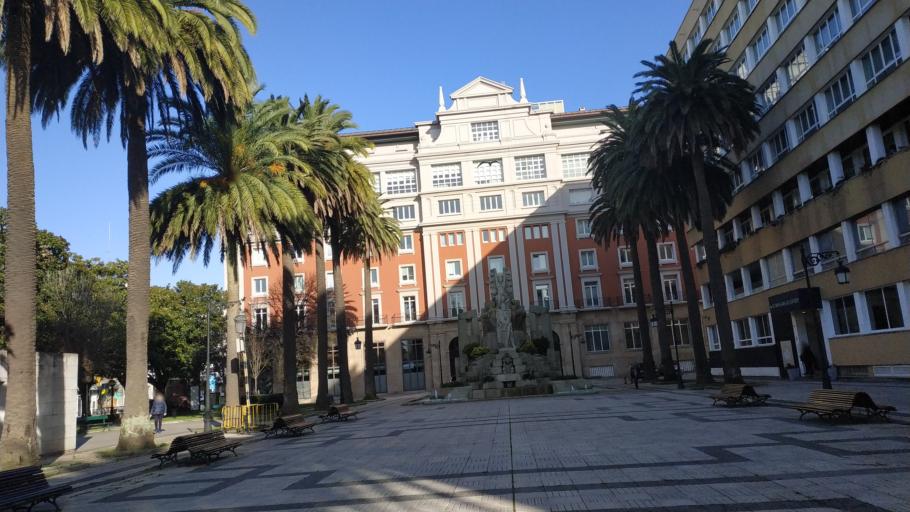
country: ES
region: Galicia
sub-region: Provincia da Coruna
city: A Coruna
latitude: 43.3684
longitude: -8.4011
